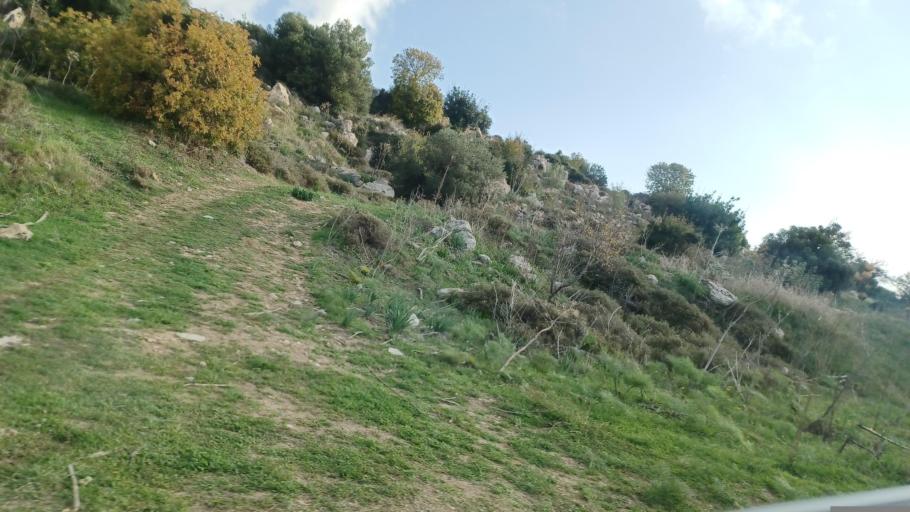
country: CY
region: Pafos
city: Mesogi
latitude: 34.7824
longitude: 32.5003
